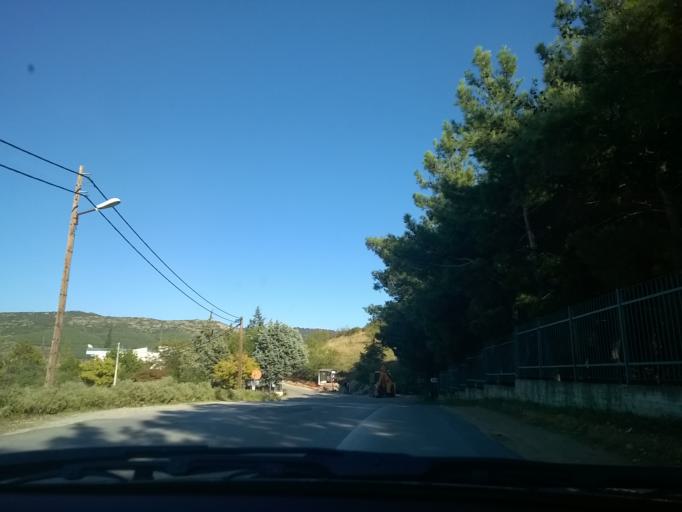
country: GR
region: Central Macedonia
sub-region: Nomos Thessalonikis
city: Polichni
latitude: 40.6654
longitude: 22.9557
